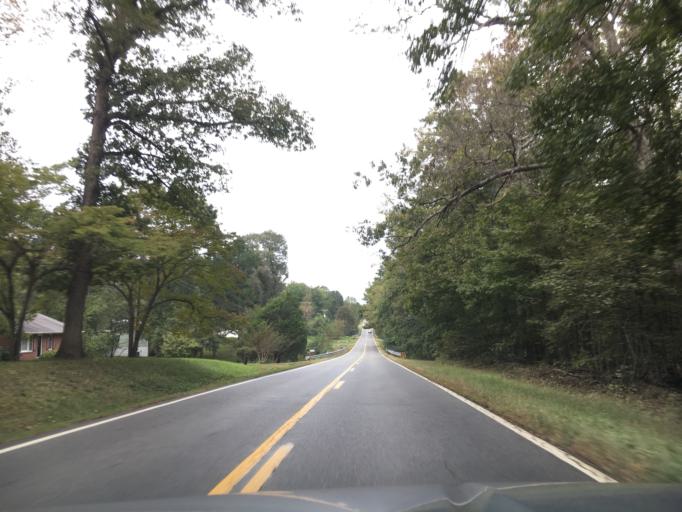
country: US
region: Virginia
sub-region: Goochland County
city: Goochland
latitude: 37.7631
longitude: -77.8785
